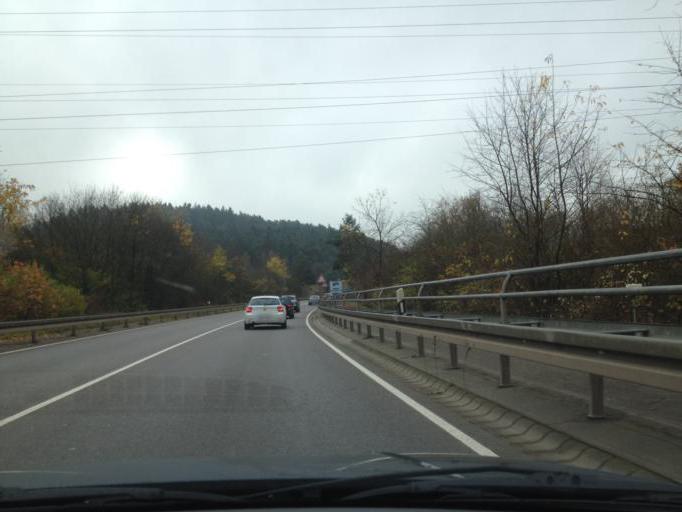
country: DE
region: Saarland
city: Bexbach
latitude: 49.3404
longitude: 7.2273
